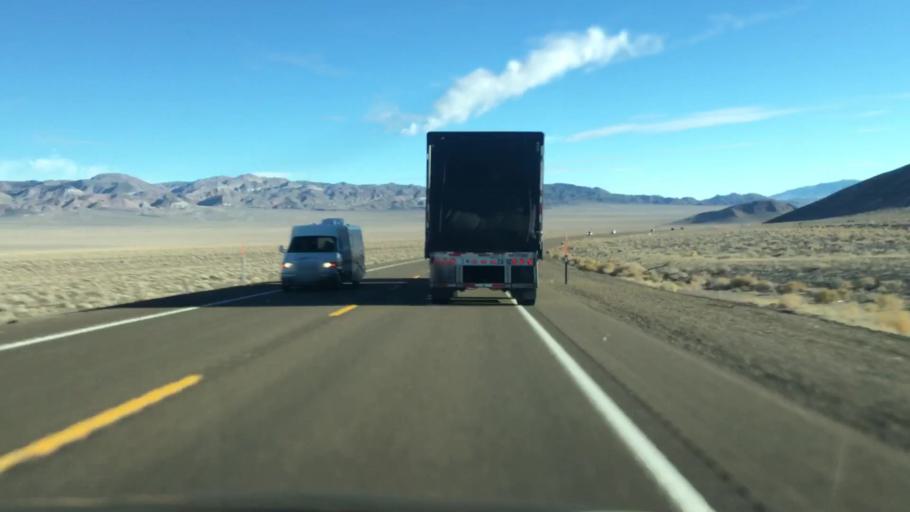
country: US
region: Nevada
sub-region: Nye County
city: Tonopah
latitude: 38.1738
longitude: -117.9600
